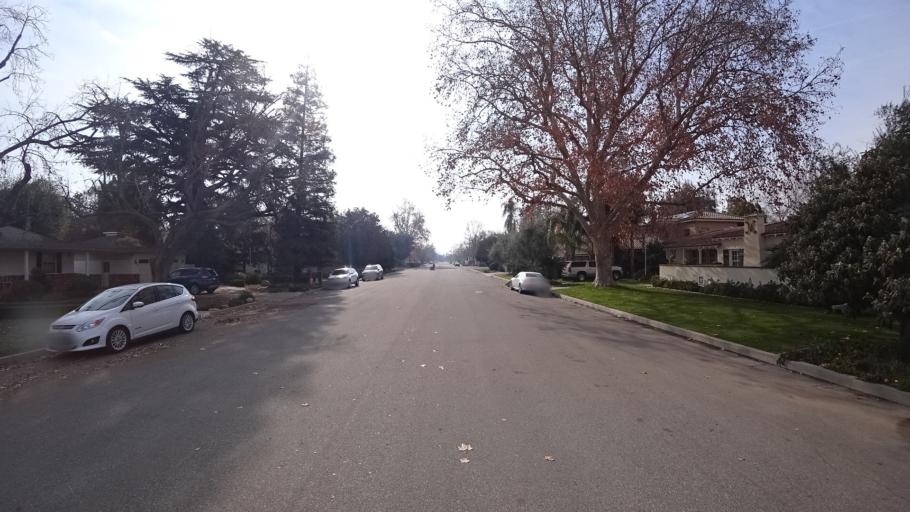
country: US
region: California
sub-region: Kern County
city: Bakersfield
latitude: 35.3801
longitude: -119.0328
